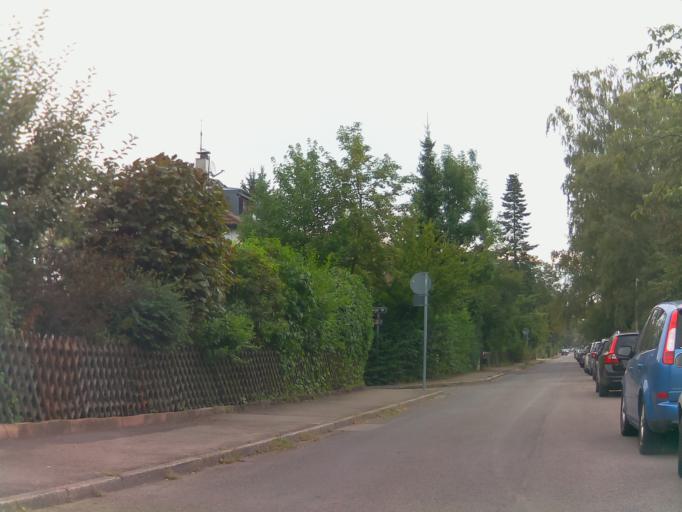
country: DE
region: Baden-Wuerttemberg
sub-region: Regierungsbezirk Stuttgart
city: Leinfelden-Echterdingen
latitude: 48.7392
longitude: 9.1461
